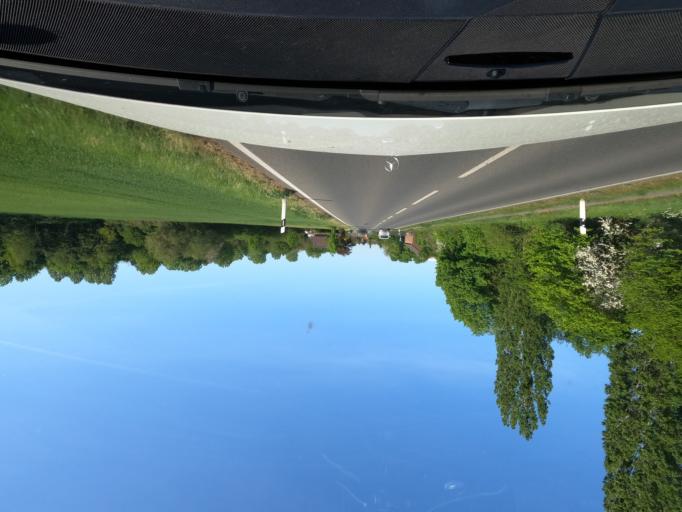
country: DE
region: North Rhine-Westphalia
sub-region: Regierungsbezirk Dusseldorf
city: Moers
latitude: 51.4799
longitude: 6.6007
